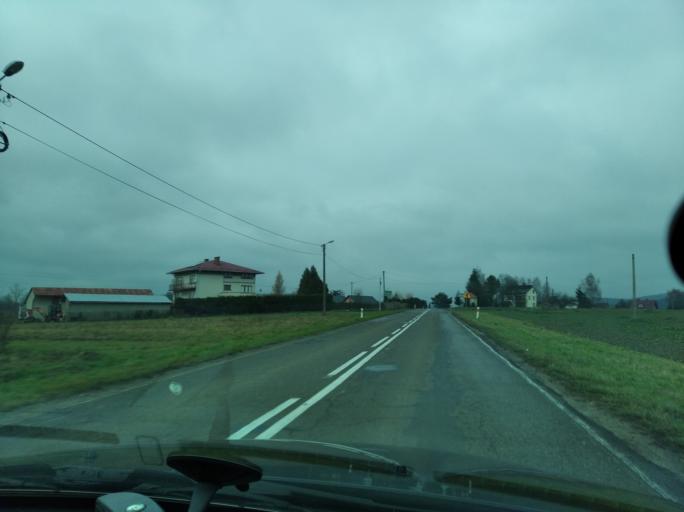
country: PL
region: Subcarpathian Voivodeship
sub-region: Powiat rzeszowski
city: Dynow
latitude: 49.8440
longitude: 22.2436
